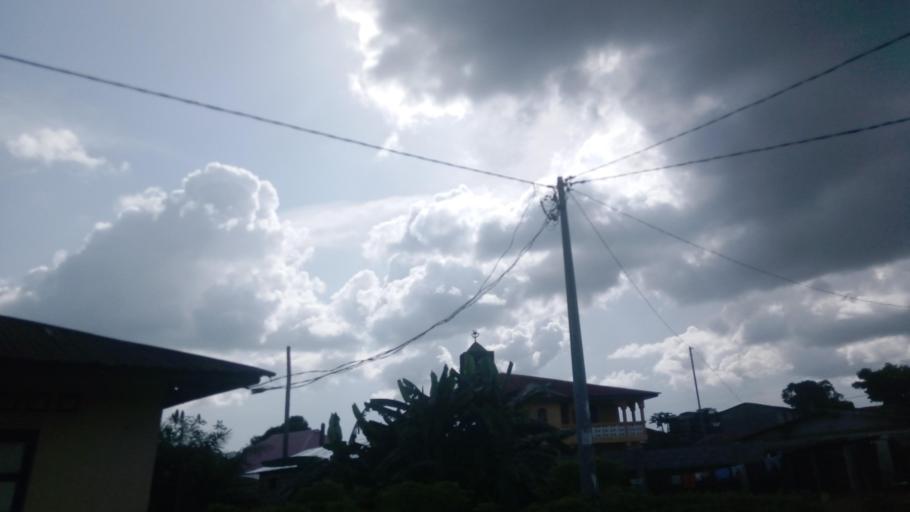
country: SL
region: Northern Province
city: Makeni
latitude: 8.8921
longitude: -12.0469
